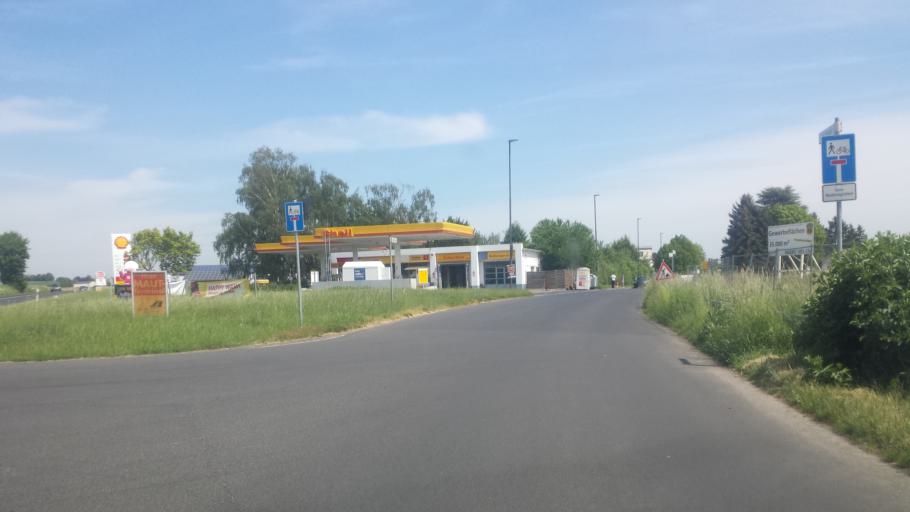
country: DE
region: Hesse
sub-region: Regierungsbezirk Darmstadt
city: Karben
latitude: 50.2425
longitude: 8.7478
